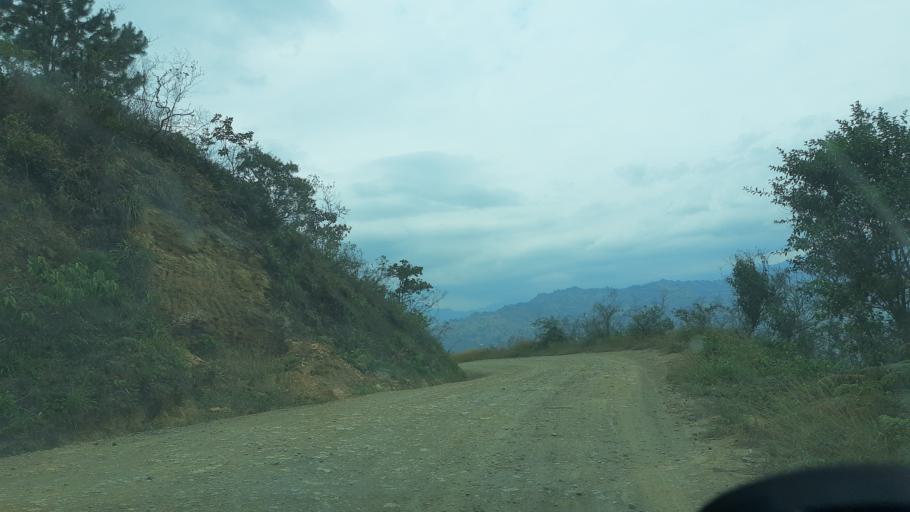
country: CO
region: Boyaca
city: Somondoco
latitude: 4.9853
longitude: -73.3757
